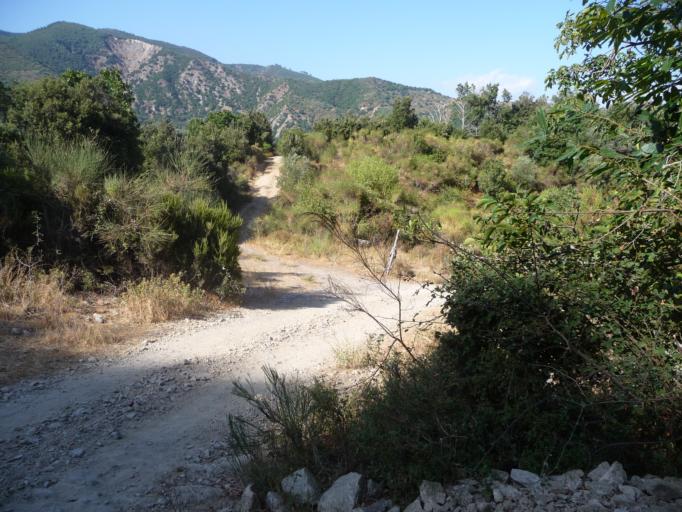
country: IT
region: Calabria
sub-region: Provincia di Reggio Calabria
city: Bivongi
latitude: 38.4872
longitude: 16.4149
